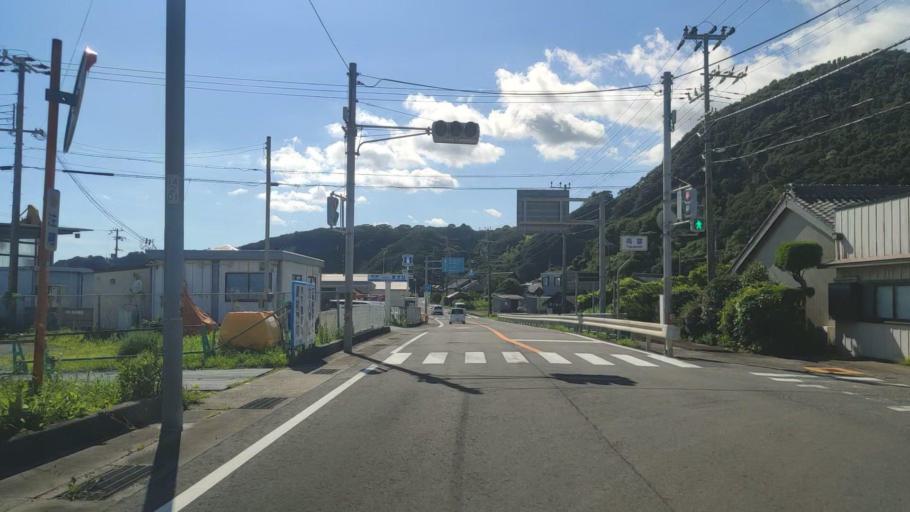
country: JP
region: Wakayama
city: Shingu
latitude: 33.4836
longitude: 135.7623
